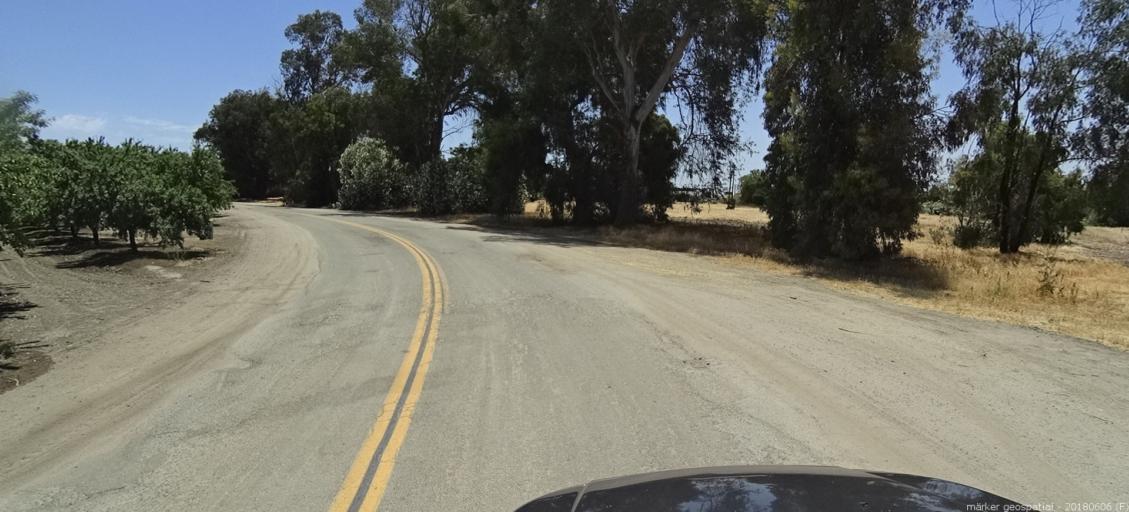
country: US
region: California
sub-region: Fresno County
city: Firebaugh
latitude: 36.8431
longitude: -120.4177
